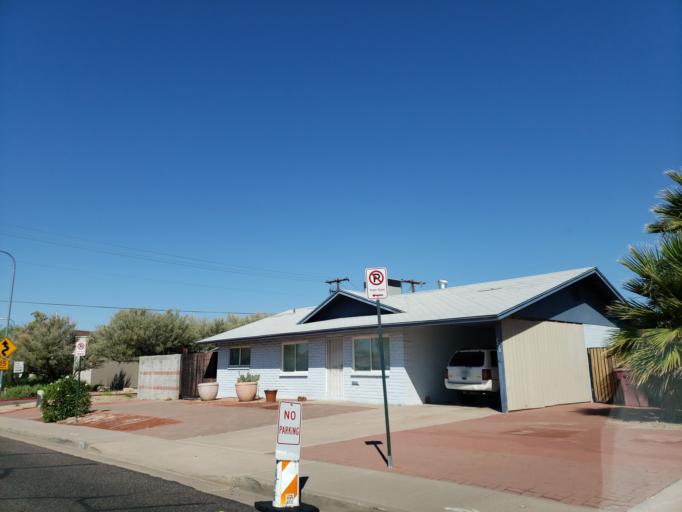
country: US
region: Arizona
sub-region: Maricopa County
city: Tempe
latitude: 33.4586
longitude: -111.9129
